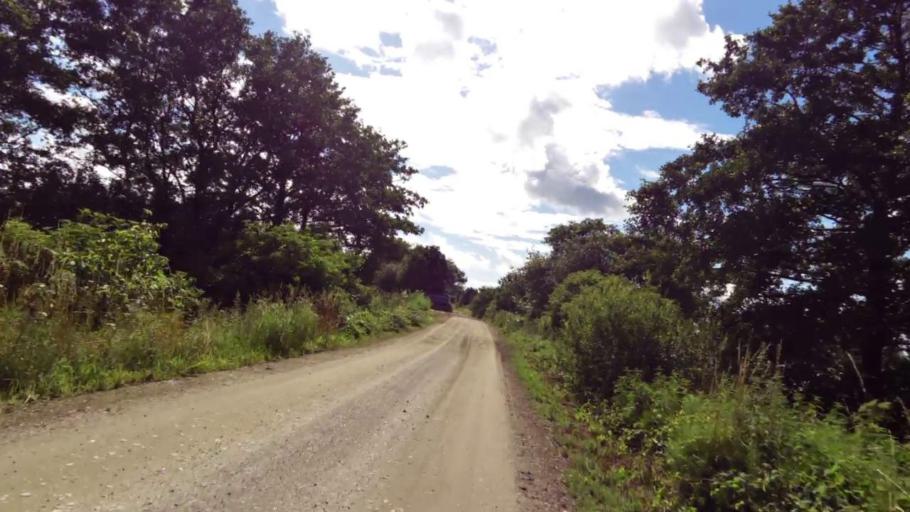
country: PL
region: West Pomeranian Voivodeship
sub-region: Powiat slawienski
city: Slawno
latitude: 54.5163
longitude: 16.7166
